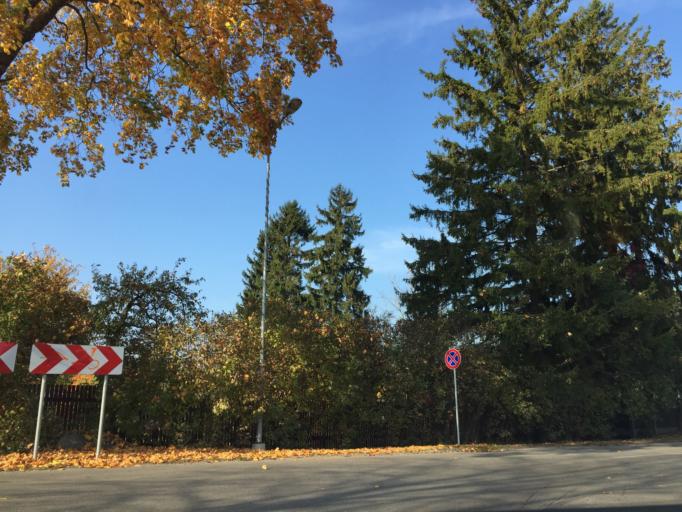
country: LV
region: Marupe
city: Marupe
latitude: 56.8908
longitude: 24.0461
